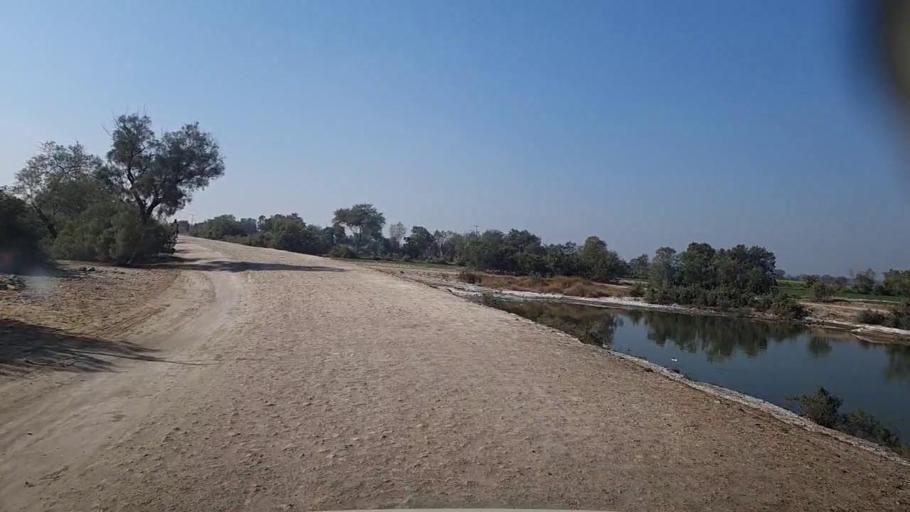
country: PK
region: Sindh
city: Khairpur
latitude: 27.9547
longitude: 69.6836
